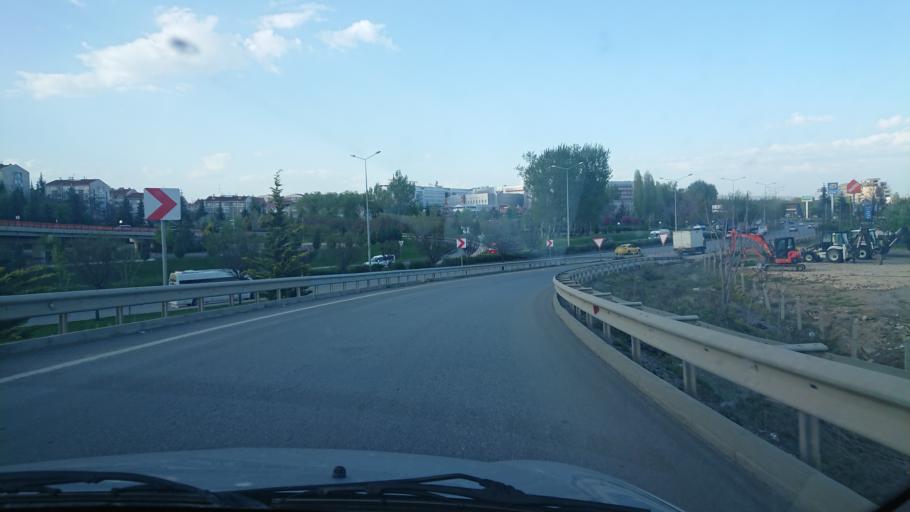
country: TR
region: Eskisehir
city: Eskisehir
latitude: 39.7806
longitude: 30.4847
